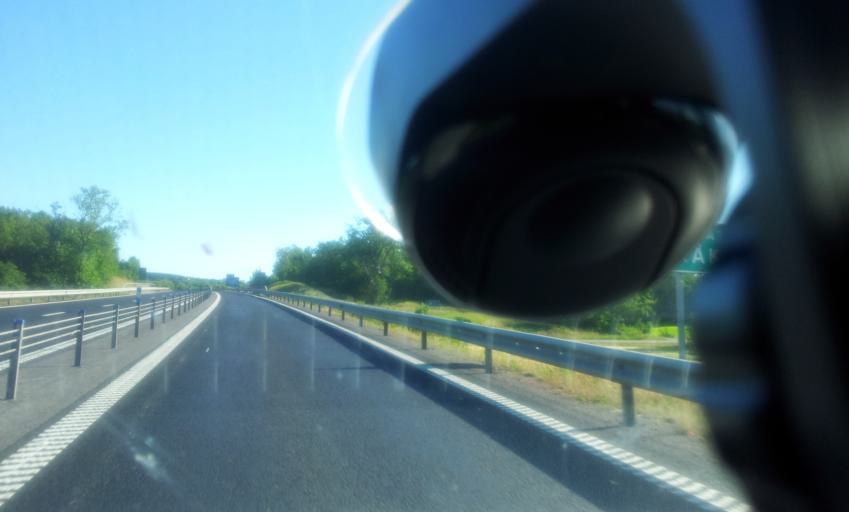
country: SE
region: Kalmar
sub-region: Torsas Kommun
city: Torsas
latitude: 56.4392
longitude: 16.0773
